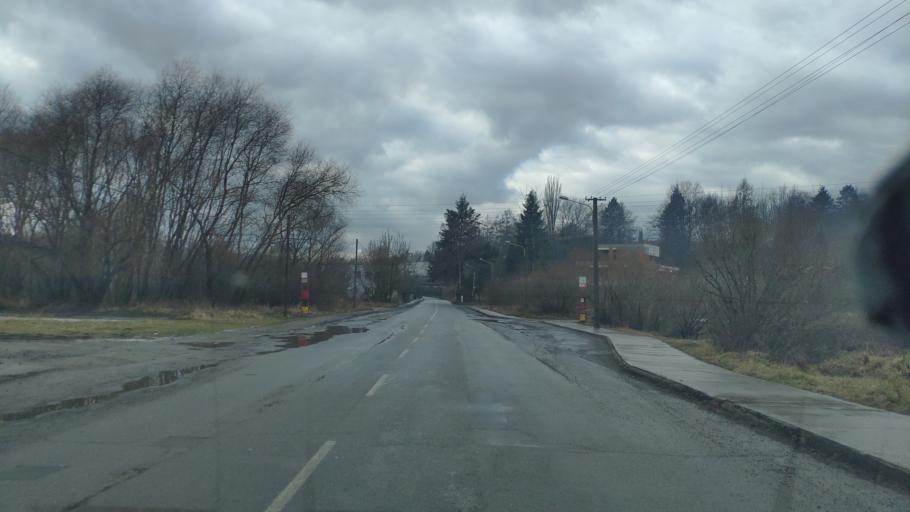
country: SK
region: Presovsky
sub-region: Okres Presov
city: Presov
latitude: 48.9931
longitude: 21.2593
